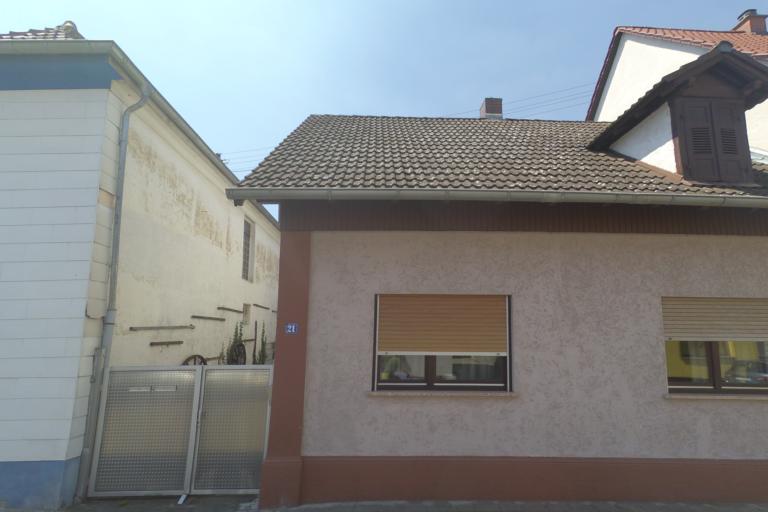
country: DE
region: Rheinland-Pfalz
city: Gartenstadt
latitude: 49.4909
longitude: 8.3725
